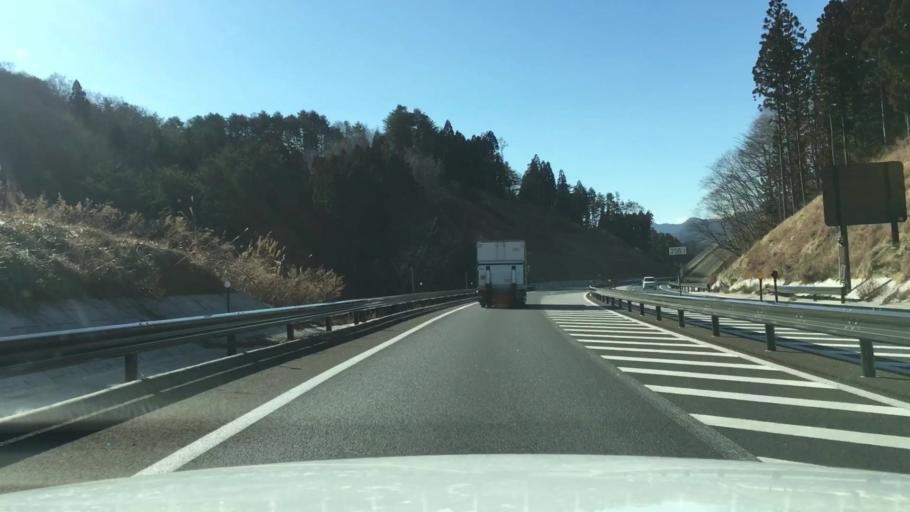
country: JP
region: Iwate
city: Miyako
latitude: 39.5901
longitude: 141.9401
